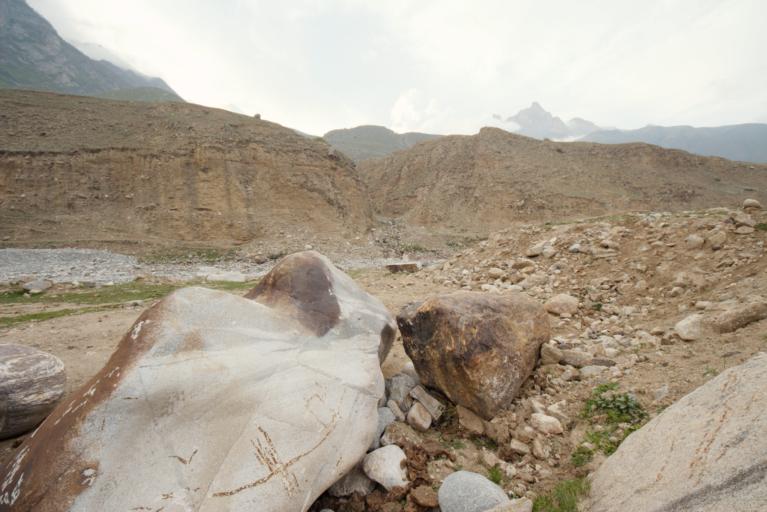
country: RU
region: Kabardino-Balkariya
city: Verkhnyaya Balkariya
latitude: 43.1170
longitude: 43.4379
